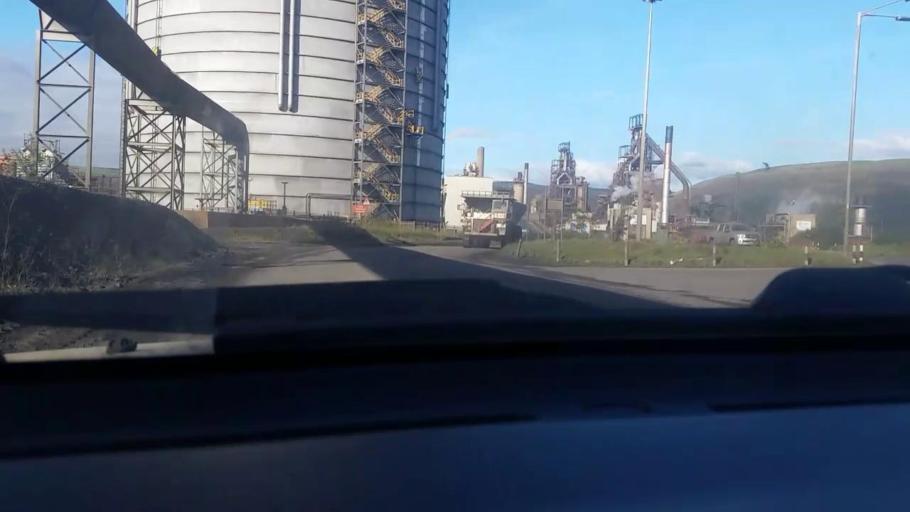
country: GB
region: Wales
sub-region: Neath Port Talbot
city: Taibach
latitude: 51.5728
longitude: -3.7791
